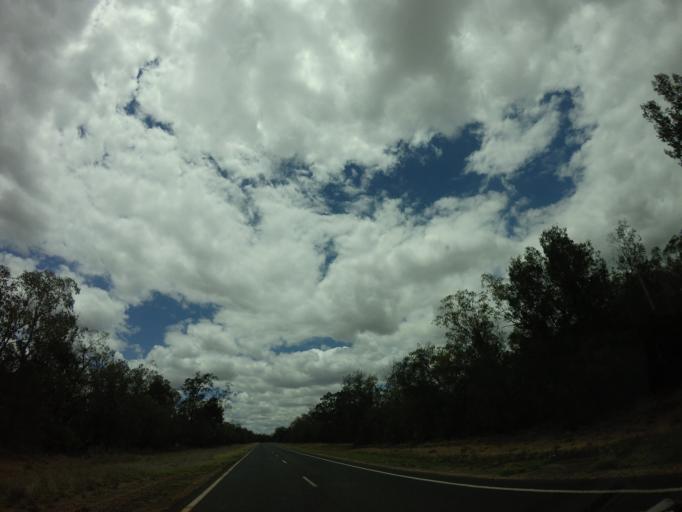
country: AU
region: Queensland
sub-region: Goondiwindi
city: Goondiwindi
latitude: -28.1607
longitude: 150.6290
